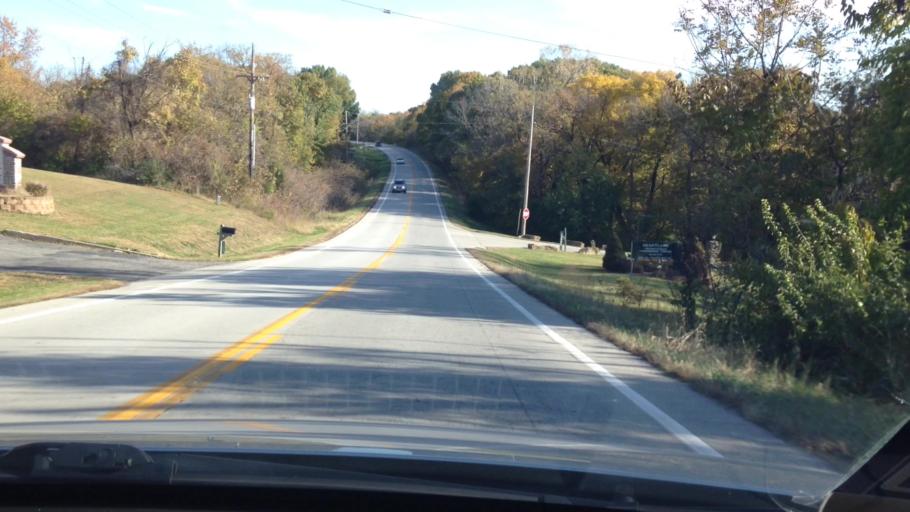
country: US
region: Missouri
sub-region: Platte County
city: Weatherby Lake
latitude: 39.2296
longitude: -94.7788
